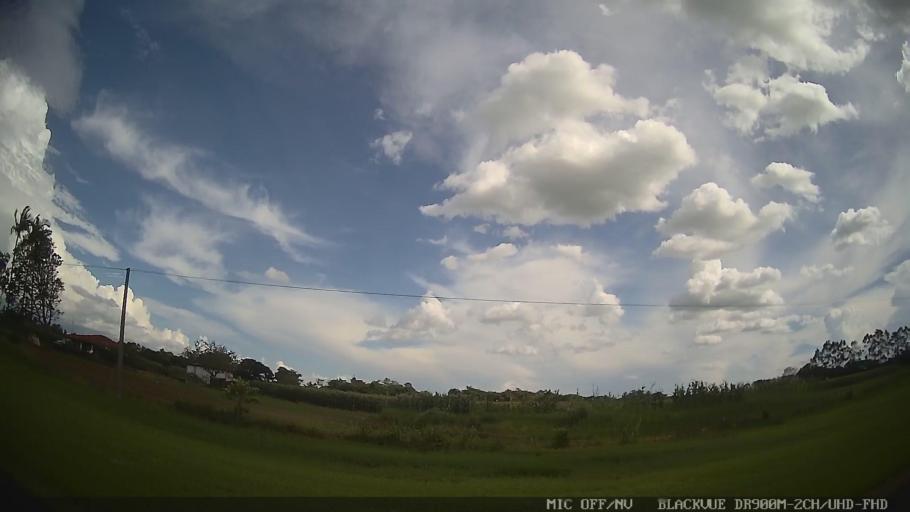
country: BR
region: Sao Paulo
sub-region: Laranjal Paulista
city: Laranjal Paulista
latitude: -23.0460
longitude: -47.9188
